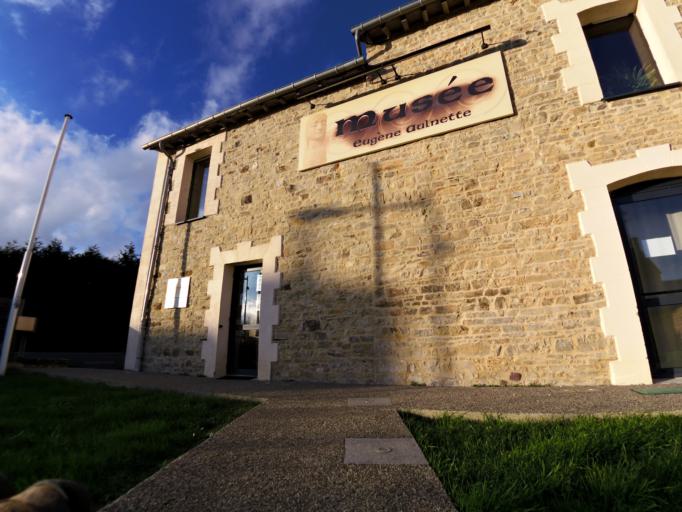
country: FR
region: Brittany
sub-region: Departement d'Ille-et-Vilaine
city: Pance
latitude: 47.8963
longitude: -1.6083
